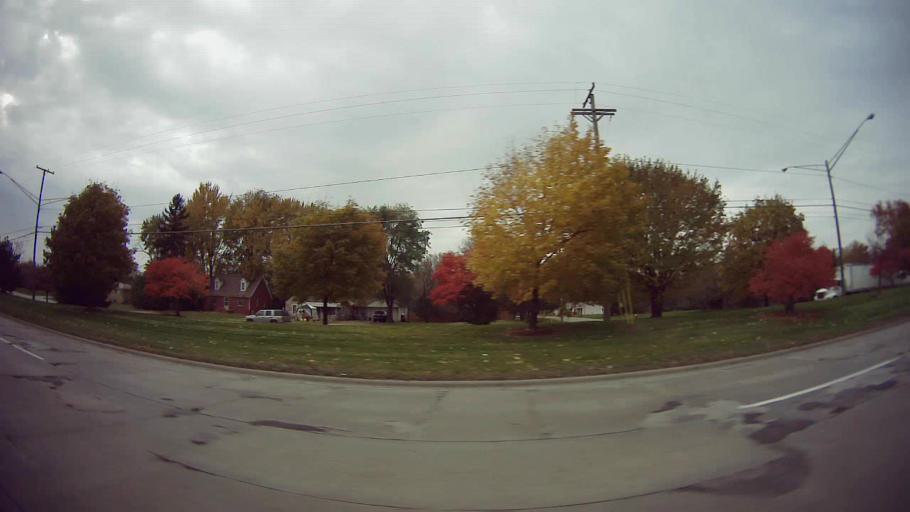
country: US
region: Michigan
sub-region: Macomb County
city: Sterling Heights
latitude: 42.5436
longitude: -83.0478
